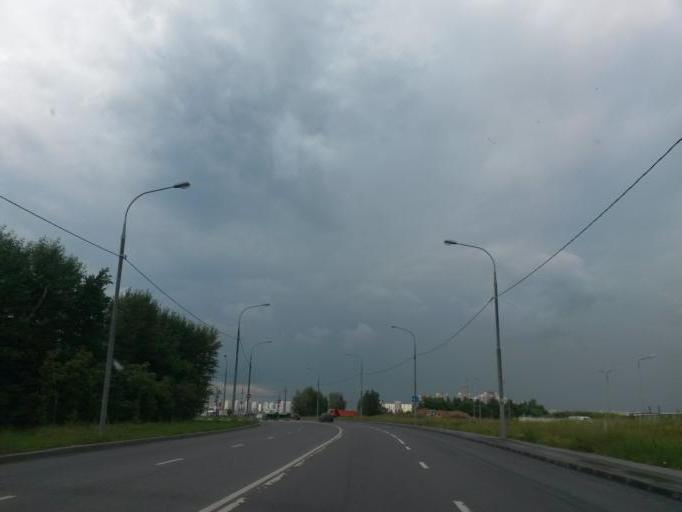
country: RU
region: Moskovskaya
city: Shcherbinka
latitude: 55.5174
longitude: 37.5774
